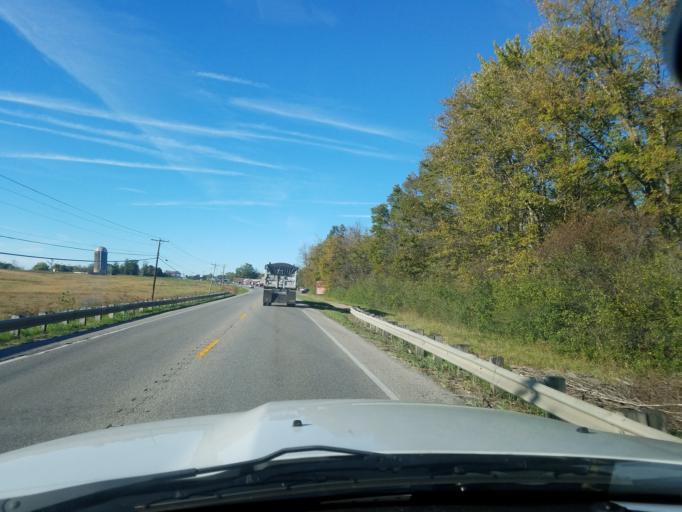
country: US
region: Kentucky
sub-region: Laurel County
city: London
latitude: 37.0808
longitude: -84.0597
